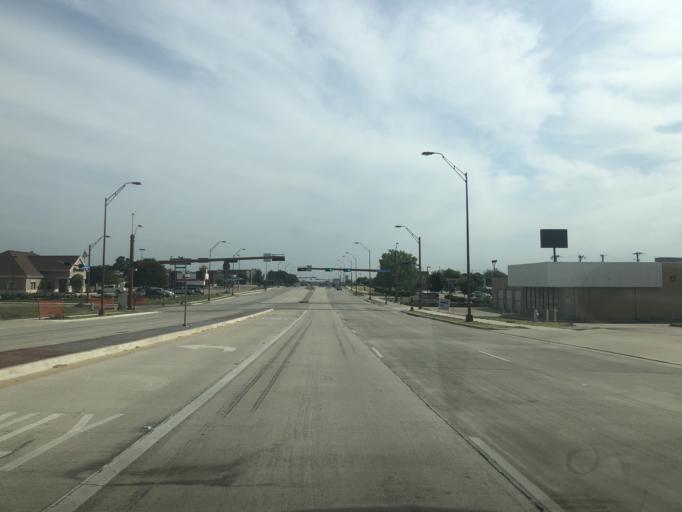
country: US
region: Texas
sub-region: Tarrant County
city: Benbrook
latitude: 32.6706
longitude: -97.4719
